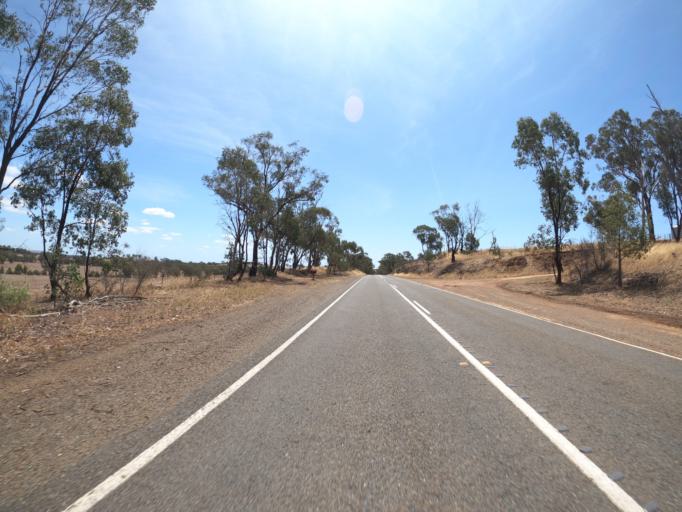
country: AU
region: Victoria
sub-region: Benalla
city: Benalla
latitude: -36.3498
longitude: 145.9624
